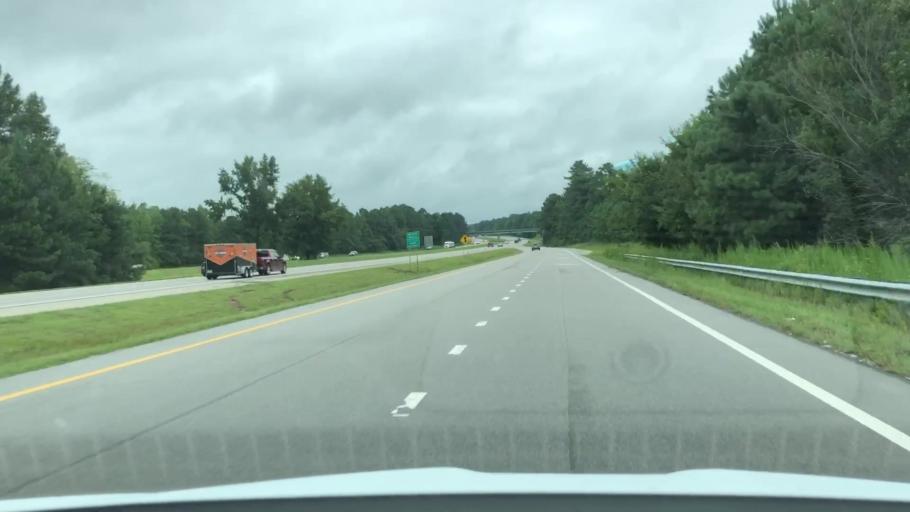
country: US
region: North Carolina
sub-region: Wilson County
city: Lucama
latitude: 35.7382
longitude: -78.0087
